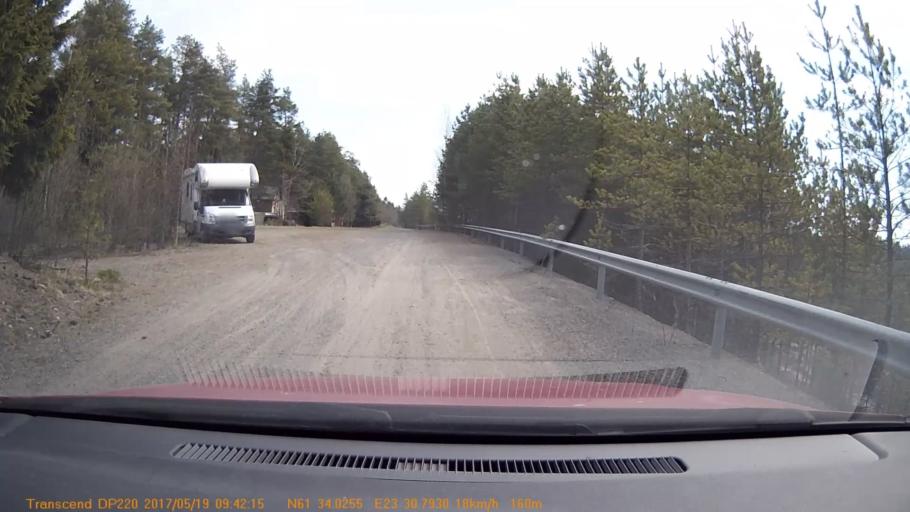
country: FI
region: Pirkanmaa
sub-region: Tampere
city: Yloejaervi
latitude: 61.5672
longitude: 23.5130
